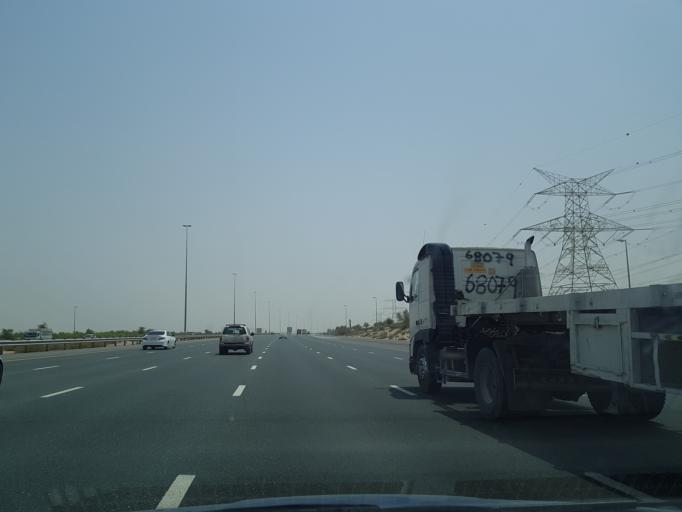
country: AE
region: Dubai
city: Dubai
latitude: 25.0611
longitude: 55.3255
